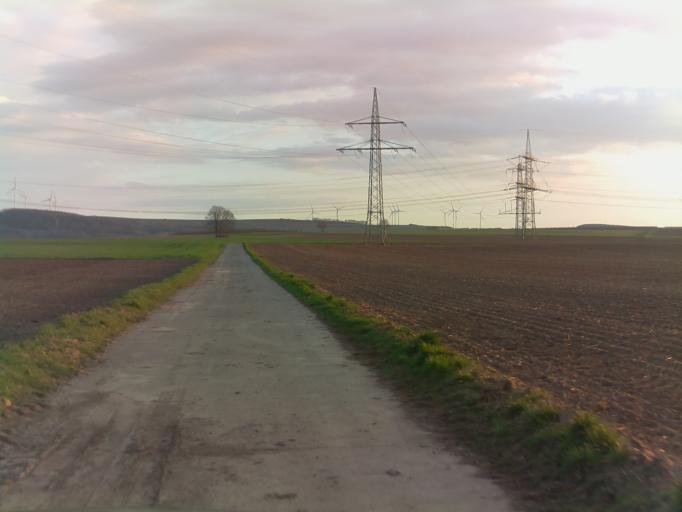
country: DE
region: Rheinland-Pfalz
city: Armsheim
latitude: 49.8089
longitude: 8.0469
